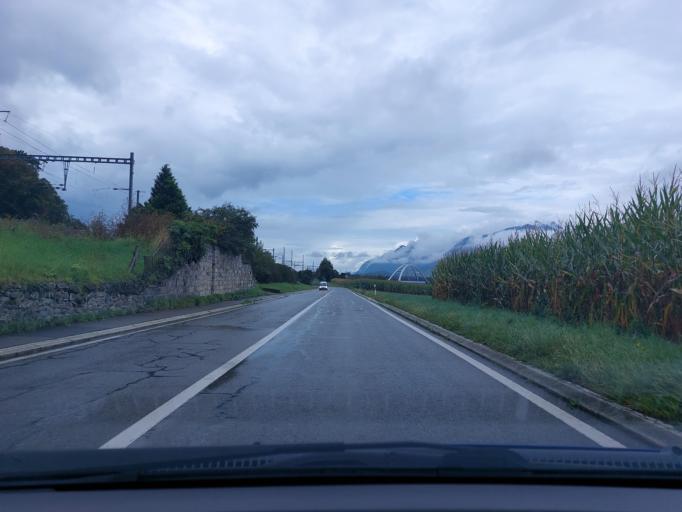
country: CH
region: Valais
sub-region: Saint-Maurice District
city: Saint-Maurice
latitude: 46.2290
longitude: 7.0010
